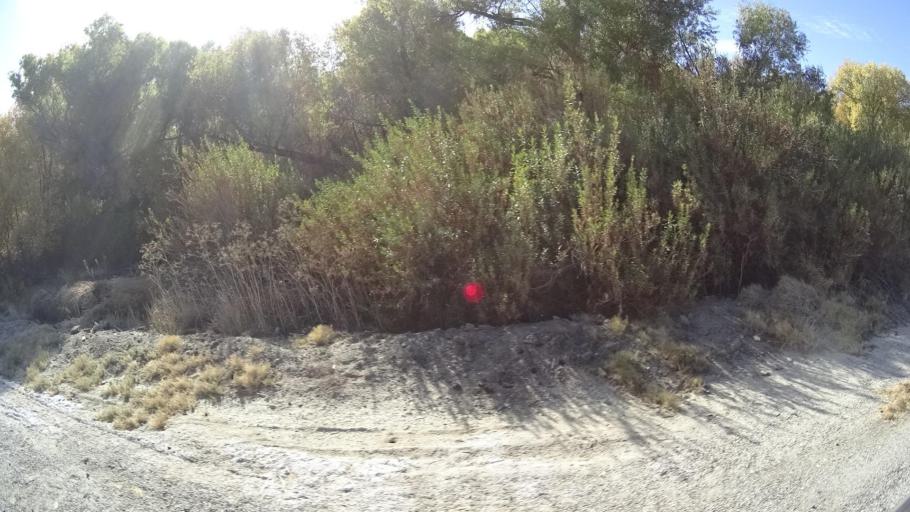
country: US
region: California
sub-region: Kern County
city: Oildale
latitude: 35.5252
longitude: -118.9486
